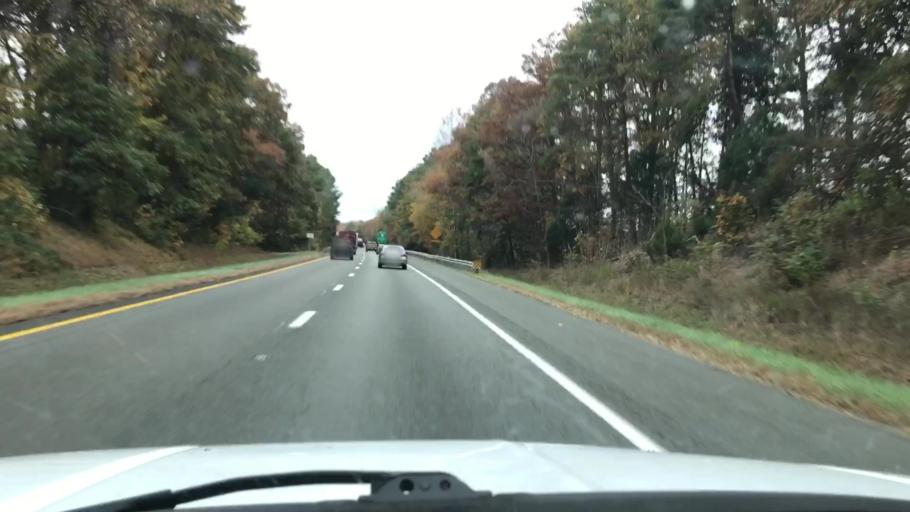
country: US
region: Virginia
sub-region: Goochland County
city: Goochland
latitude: 37.7083
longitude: -77.7730
